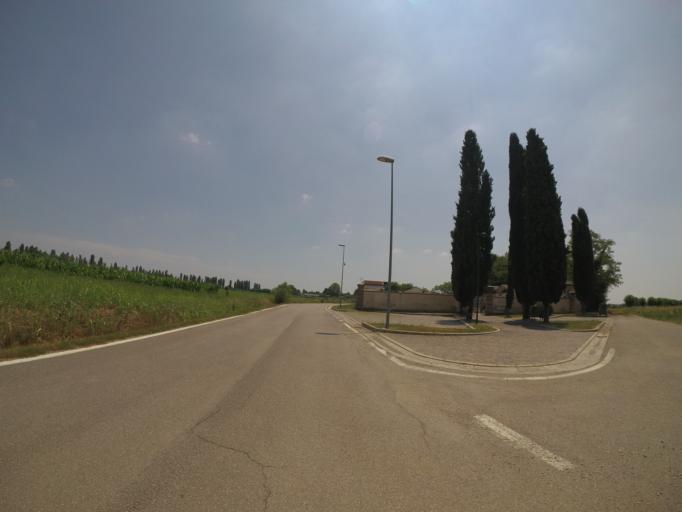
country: IT
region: Friuli Venezia Giulia
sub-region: Provincia di Udine
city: Codroipo
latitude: 45.9608
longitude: 13.0053
